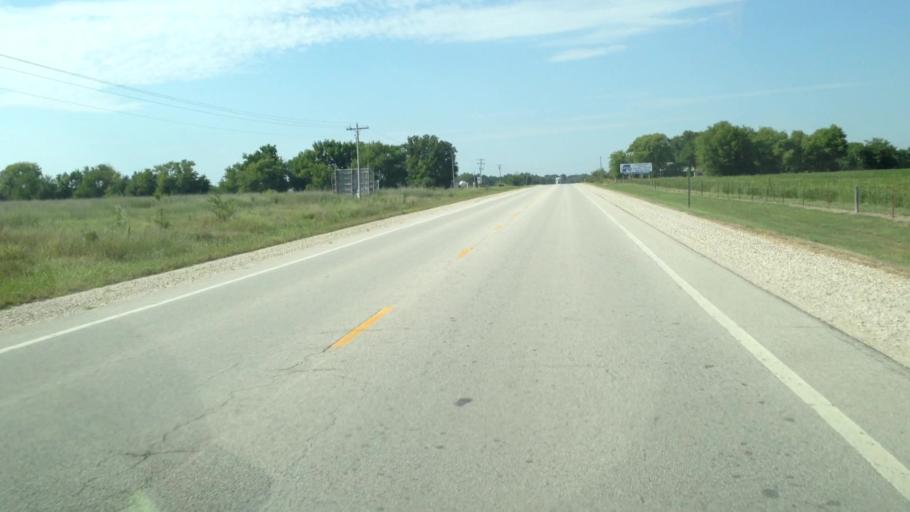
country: US
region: Kansas
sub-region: Neosho County
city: Erie
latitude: 37.5199
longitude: -95.2701
